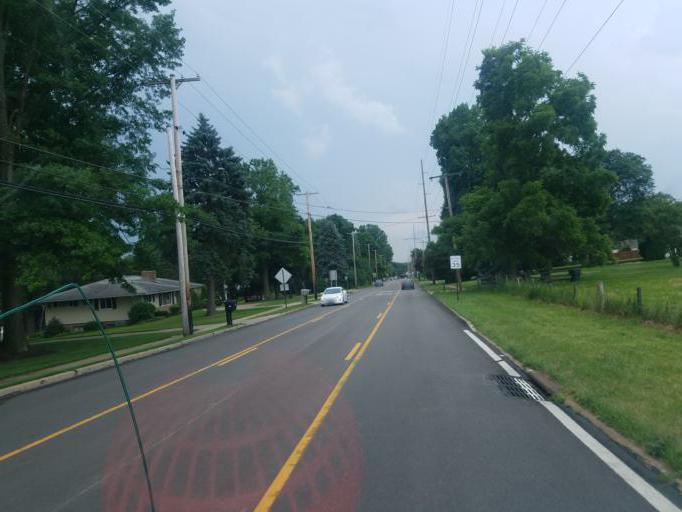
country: US
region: Ohio
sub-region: Medina County
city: Wadsworth
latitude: 41.0382
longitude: -81.7217
